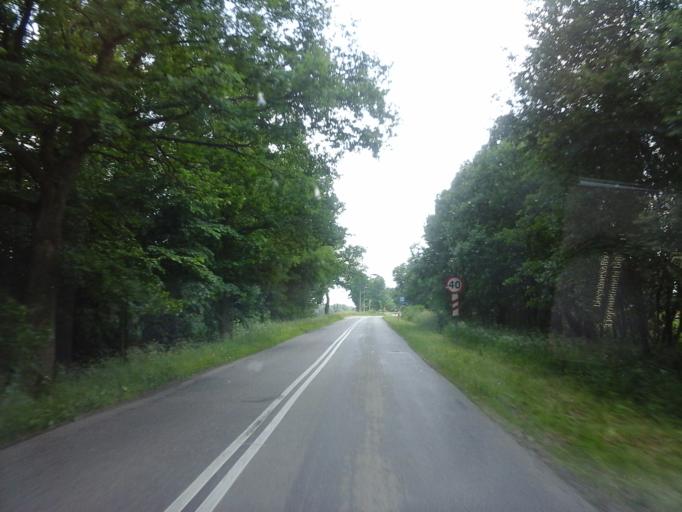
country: PL
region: West Pomeranian Voivodeship
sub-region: Powiat swidwinski
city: Swidwin
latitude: 53.7525
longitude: 15.7317
